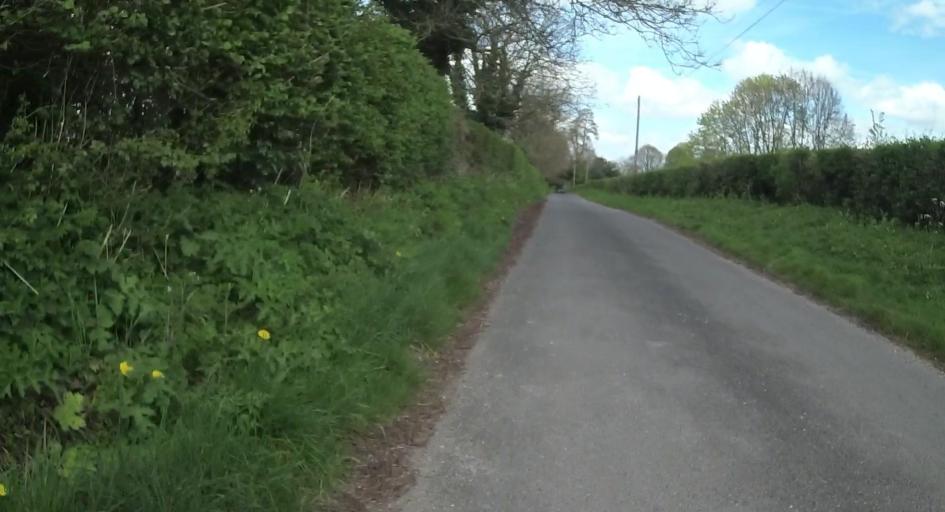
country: GB
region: England
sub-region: Hampshire
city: Romsey
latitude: 51.0753
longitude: -1.5242
